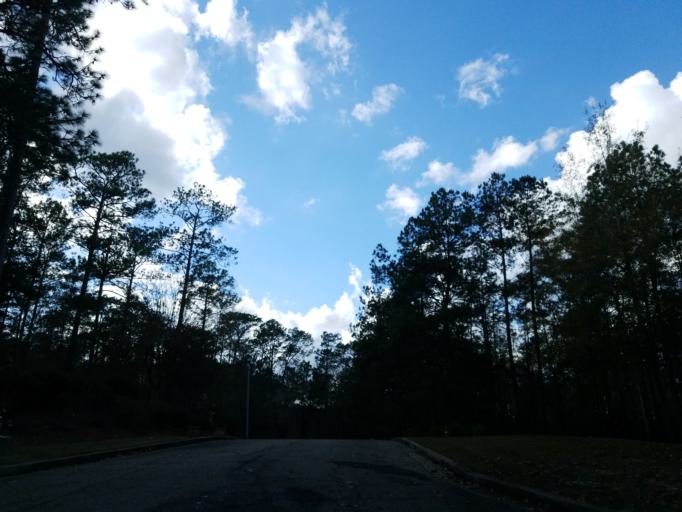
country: US
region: Mississippi
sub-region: Lamar County
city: West Hattiesburg
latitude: 31.3036
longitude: -89.3443
